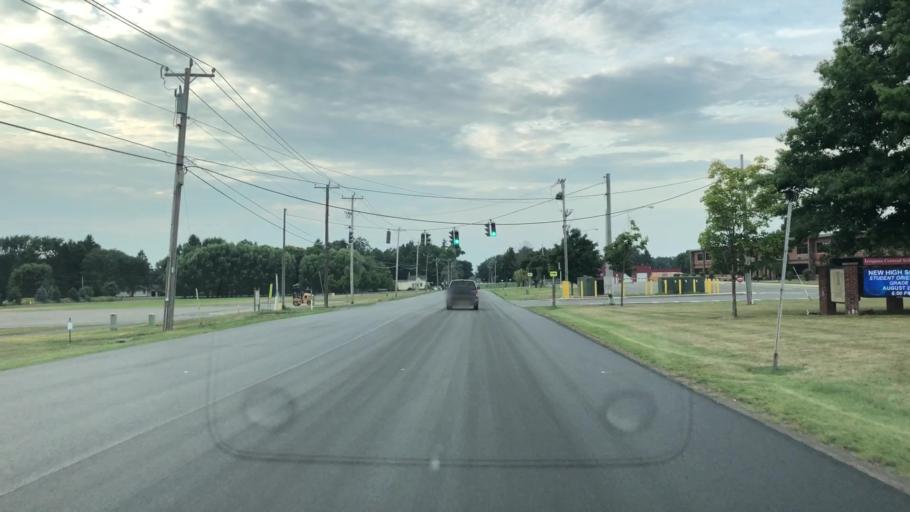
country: US
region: New York
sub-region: Erie County
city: Elma Center
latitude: 42.8347
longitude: -78.6060
